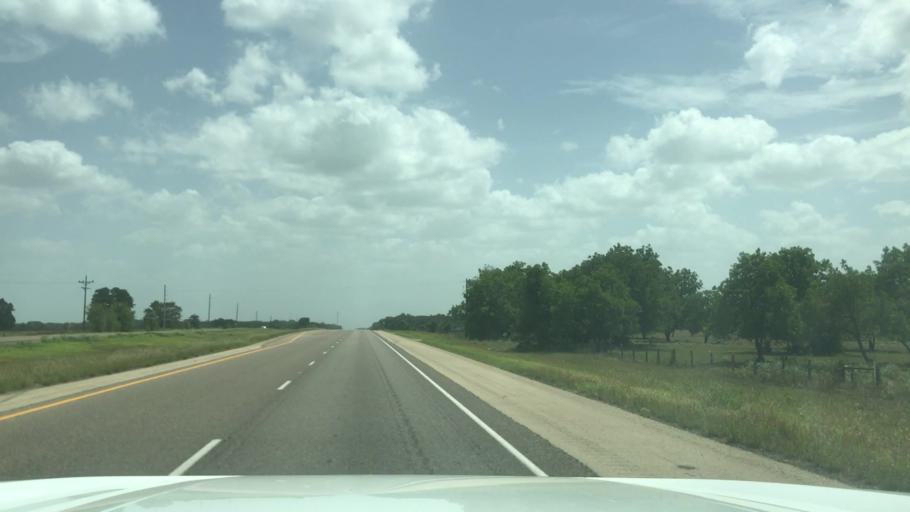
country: US
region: Texas
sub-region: Robertson County
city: Calvert
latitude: 31.0570
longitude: -96.7118
